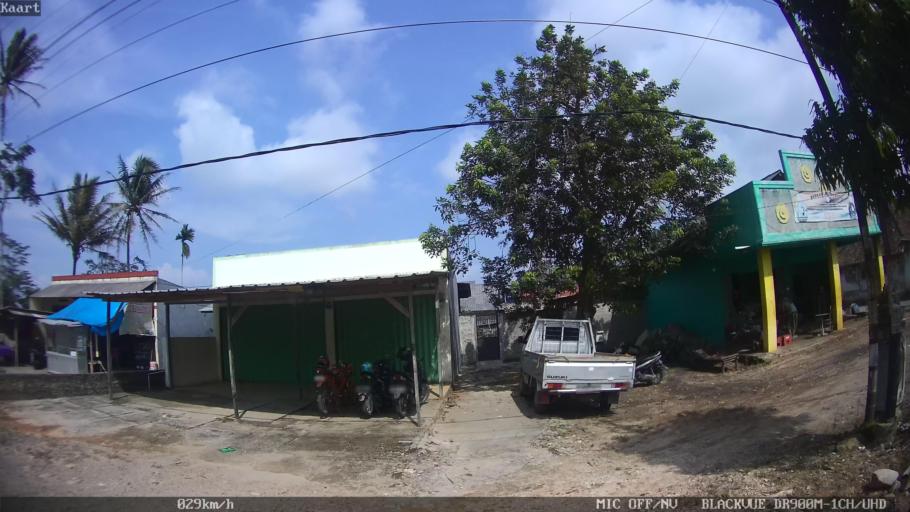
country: ID
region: Lampung
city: Kedaton
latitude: -5.3205
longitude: 105.2862
